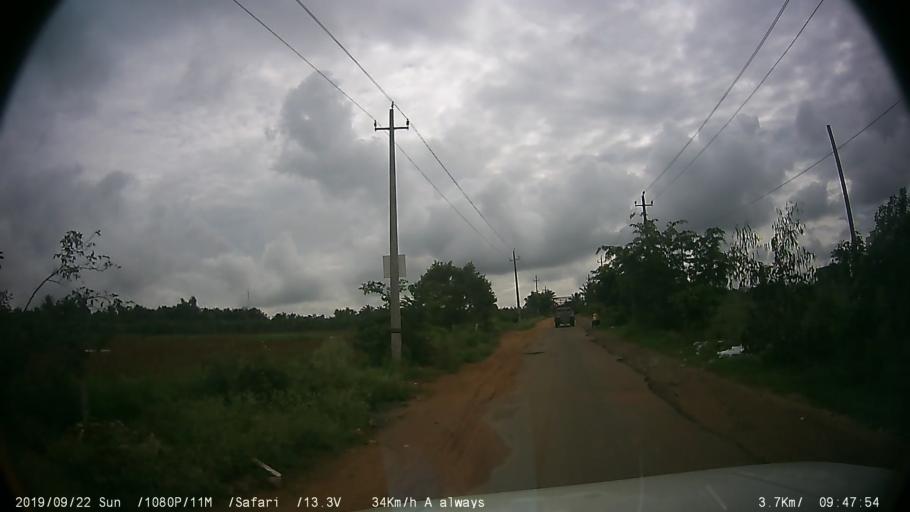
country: IN
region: Karnataka
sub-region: Bangalore Urban
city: Anekal
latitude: 12.8142
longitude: 77.6483
